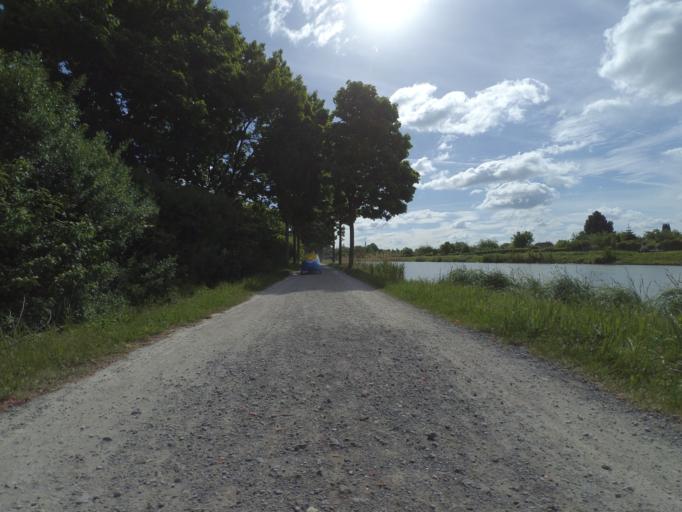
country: DE
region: Lower Saxony
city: Hannover
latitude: 52.4056
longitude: 9.7491
